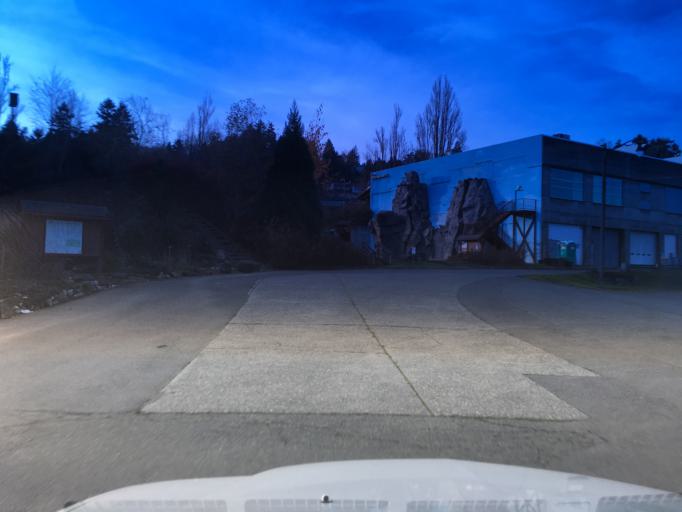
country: US
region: Washington
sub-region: King County
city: Inglewood-Finn Hill
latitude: 47.6848
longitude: -122.2630
